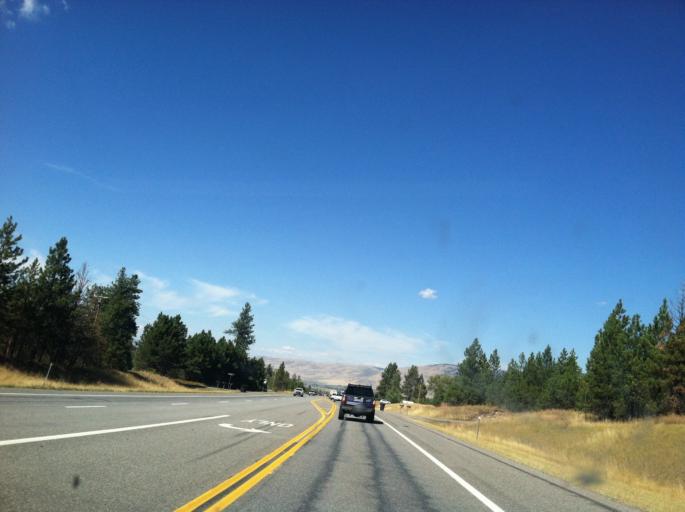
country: US
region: Montana
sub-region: Missoula County
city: Frenchtown
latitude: 47.0946
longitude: -114.0408
